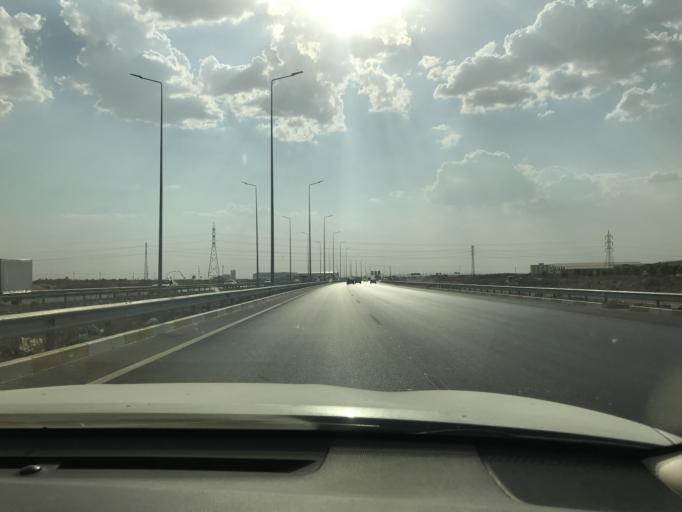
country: IQ
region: Arbil
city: Erbil
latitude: 36.1362
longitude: 43.9982
